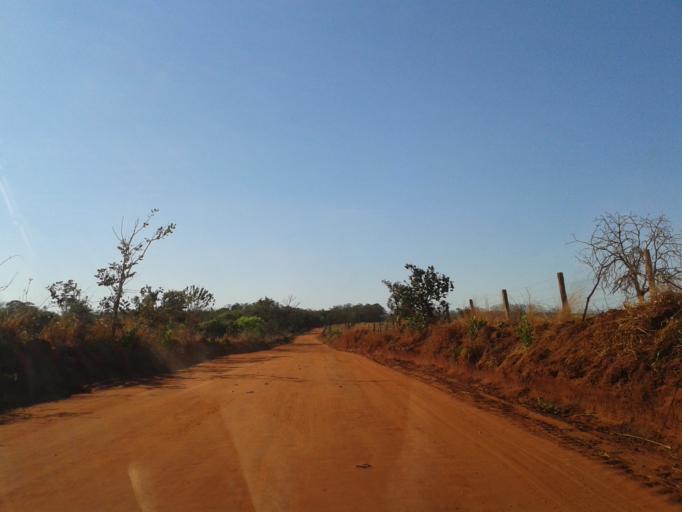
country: BR
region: Minas Gerais
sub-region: Ituiutaba
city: Ituiutaba
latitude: -18.9858
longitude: -49.3917
